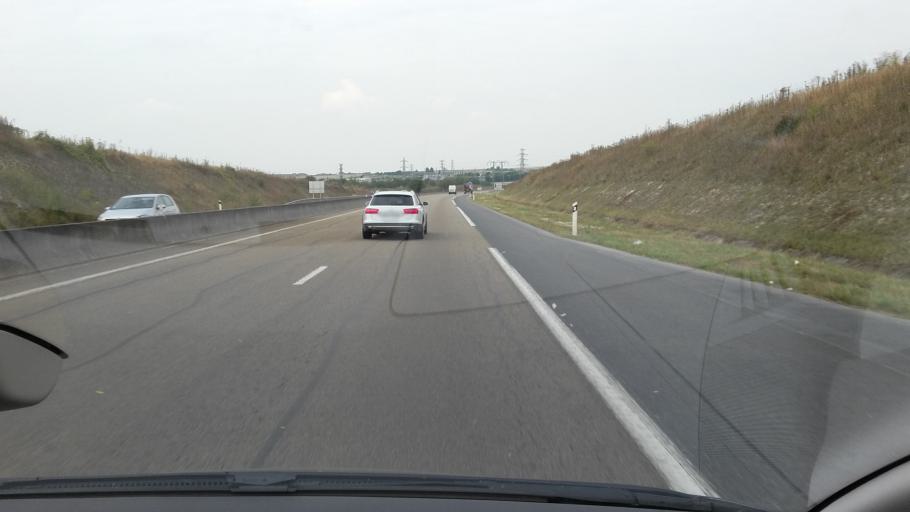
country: FR
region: Champagne-Ardenne
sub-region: Departement de la Marne
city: Cernay-les-Reims
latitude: 49.2626
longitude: 4.0858
